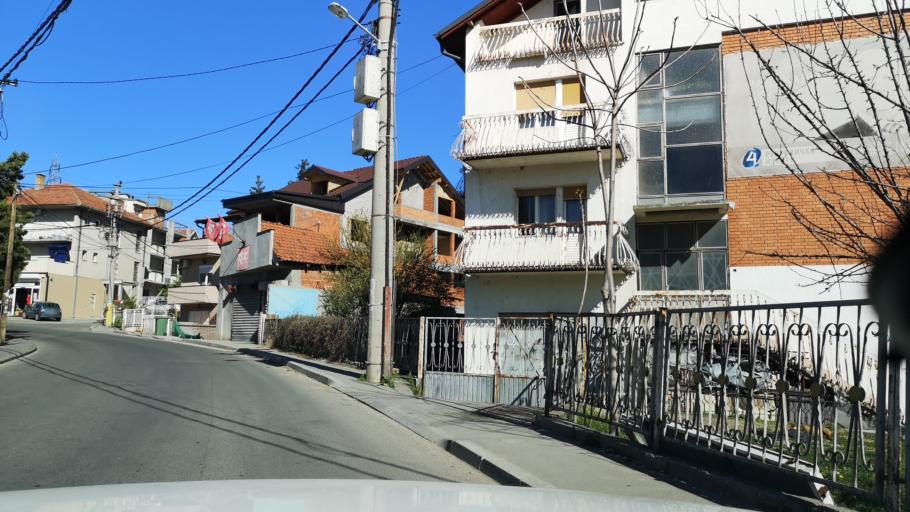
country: RS
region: Central Serbia
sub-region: Belgrade
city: Zvezdara
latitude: 44.7593
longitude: 20.5509
